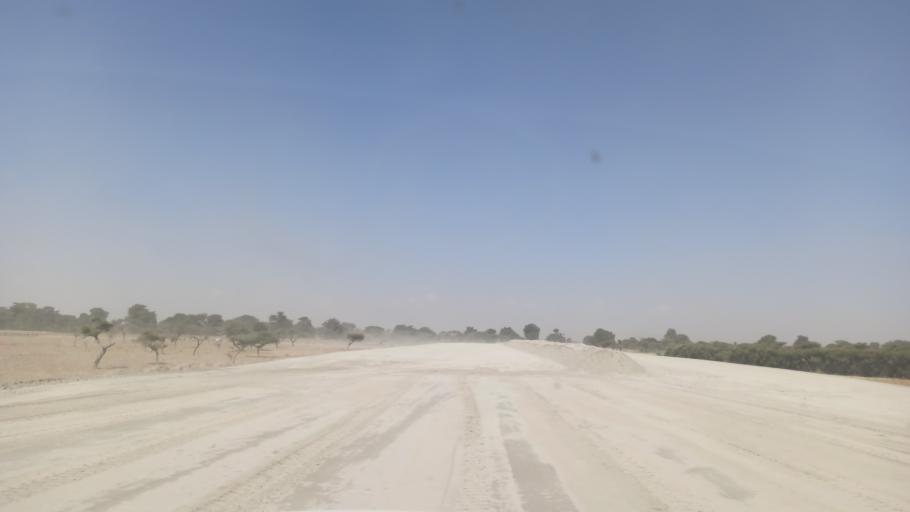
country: ET
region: Oromiya
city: Ziway
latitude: 7.6990
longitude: 38.6428
